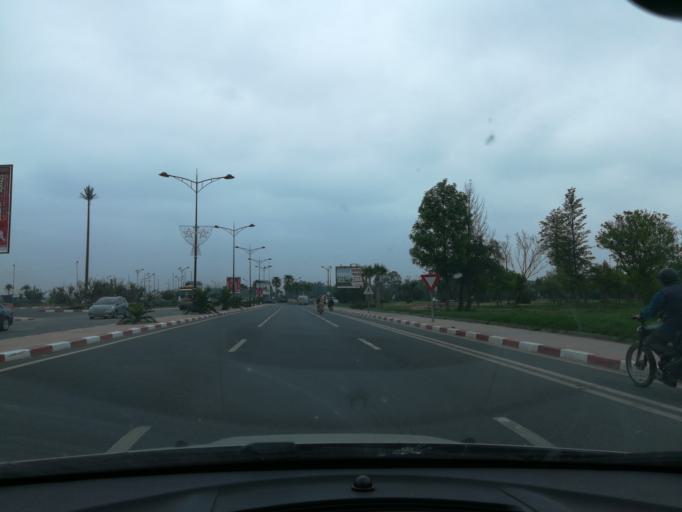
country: MA
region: Marrakech-Tensift-Al Haouz
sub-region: Marrakech
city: Marrakesh
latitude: 31.6849
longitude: -7.9933
